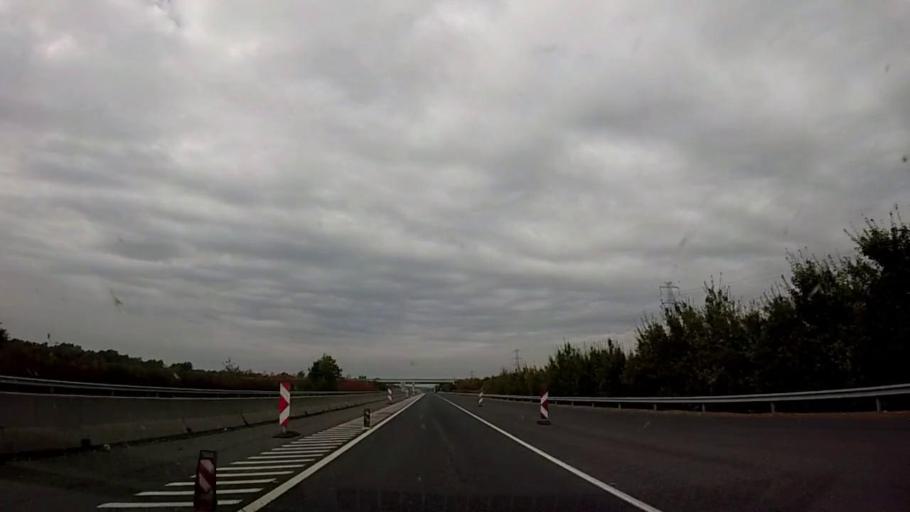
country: HR
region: Medimurska
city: Podturen
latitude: 46.5071
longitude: 16.5805
